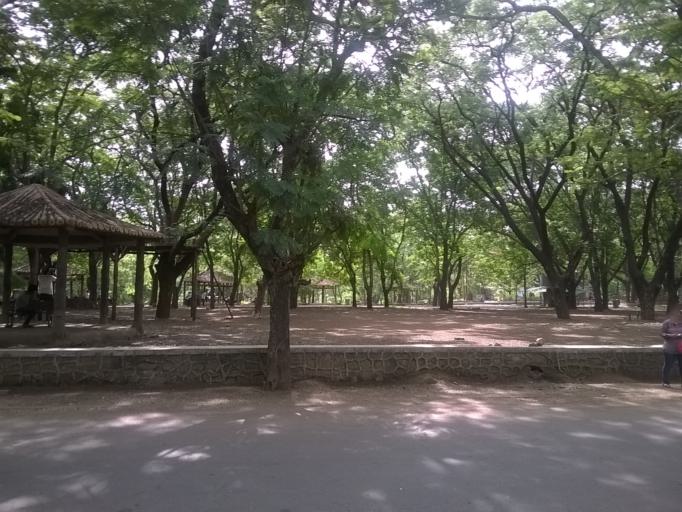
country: IN
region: Maharashtra
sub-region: Mumbai Suburban
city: Borivli
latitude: 19.2284
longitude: 72.8676
